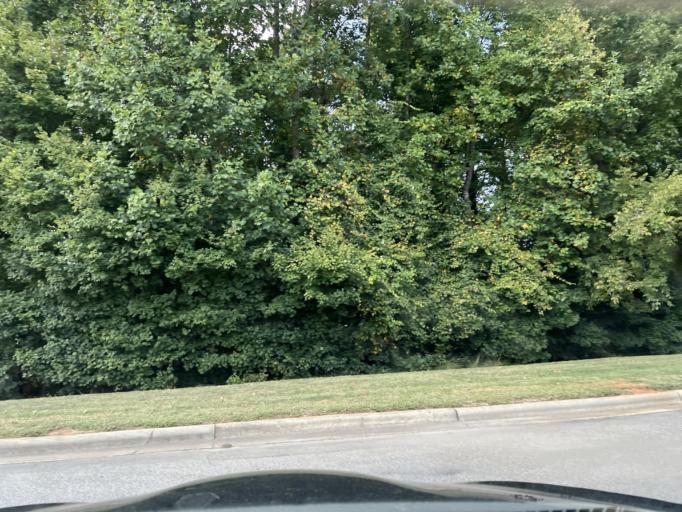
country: US
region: North Carolina
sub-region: Wake County
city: Raleigh
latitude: 35.7303
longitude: -78.6599
